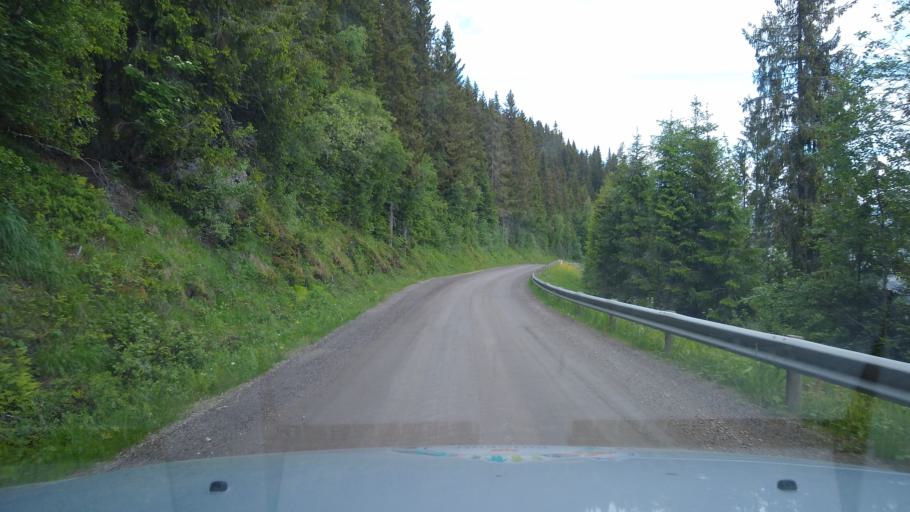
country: NO
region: Oppland
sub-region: Ringebu
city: Ringebu
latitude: 61.4983
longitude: 10.1428
